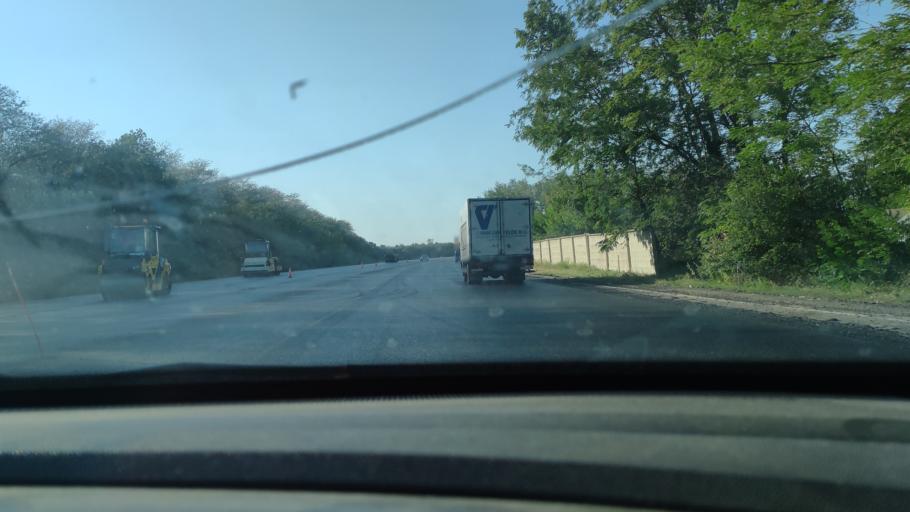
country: RU
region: Krasnodarskiy
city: Medvedovskaya
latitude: 45.5000
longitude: 38.9456
